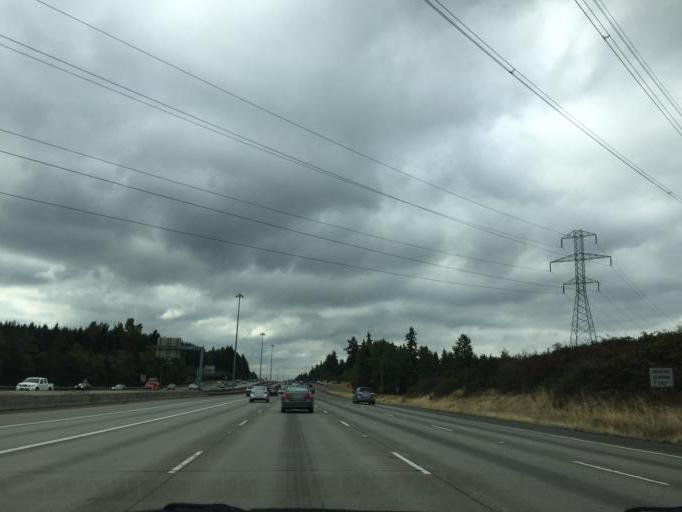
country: US
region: Washington
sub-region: King County
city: Federal Way
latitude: 47.3145
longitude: -122.2980
